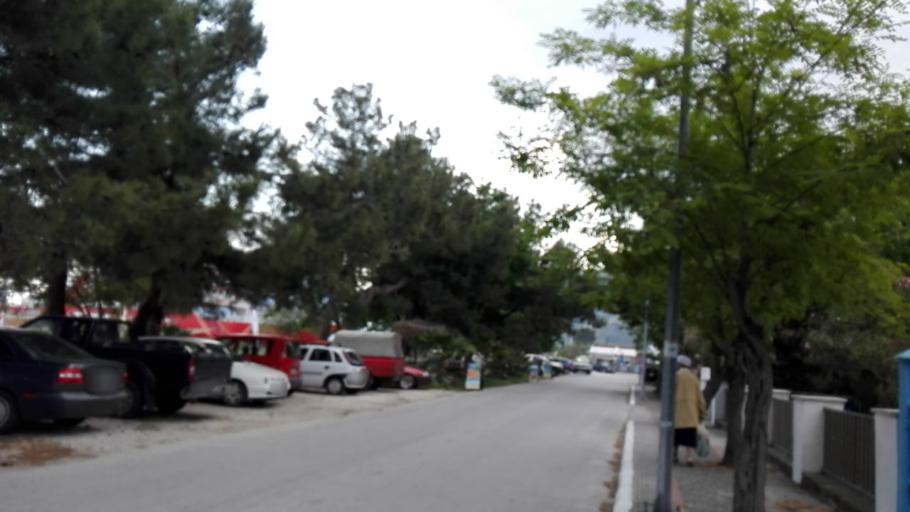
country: GR
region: East Macedonia and Thrace
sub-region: Nomos Kavalas
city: Prinos
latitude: 40.7587
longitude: 24.5750
